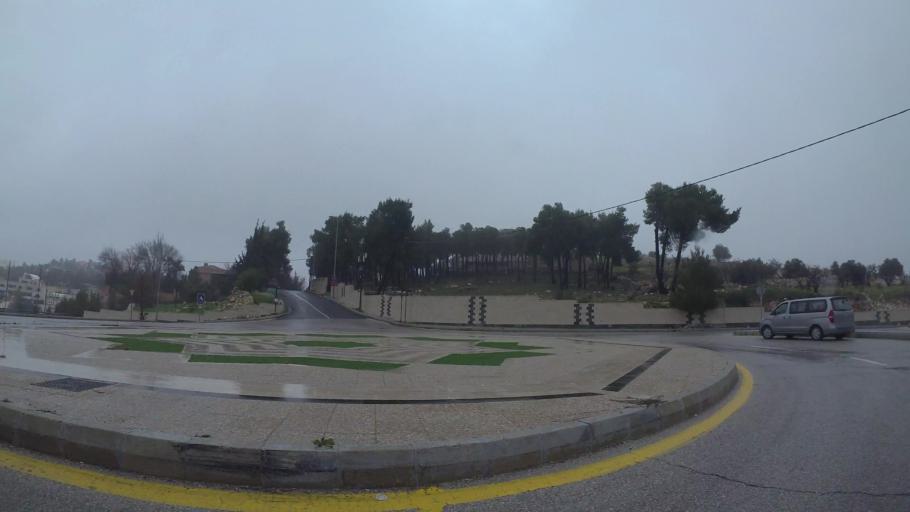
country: JO
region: Amman
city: Wadi as Sir
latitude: 32.0002
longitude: 35.8081
